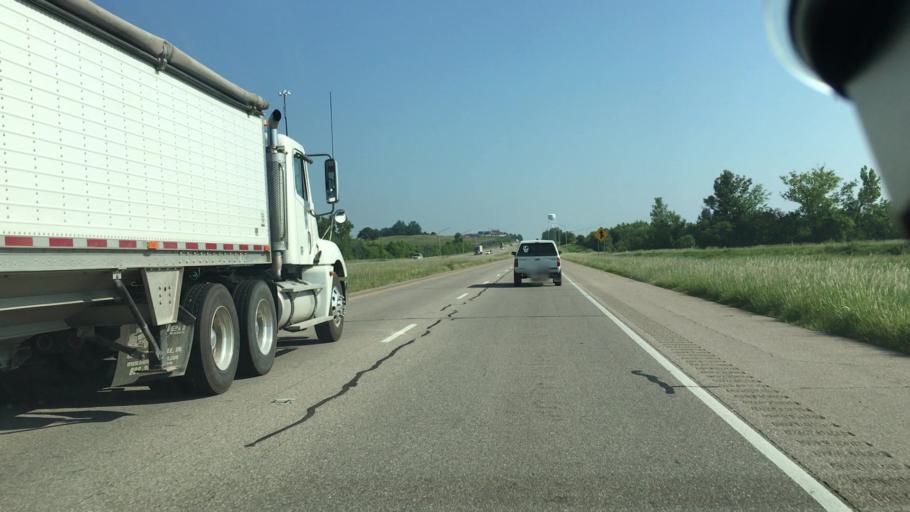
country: US
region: Indiana
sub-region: Gibson County
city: Fort Branch
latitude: 38.2751
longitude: -87.5676
